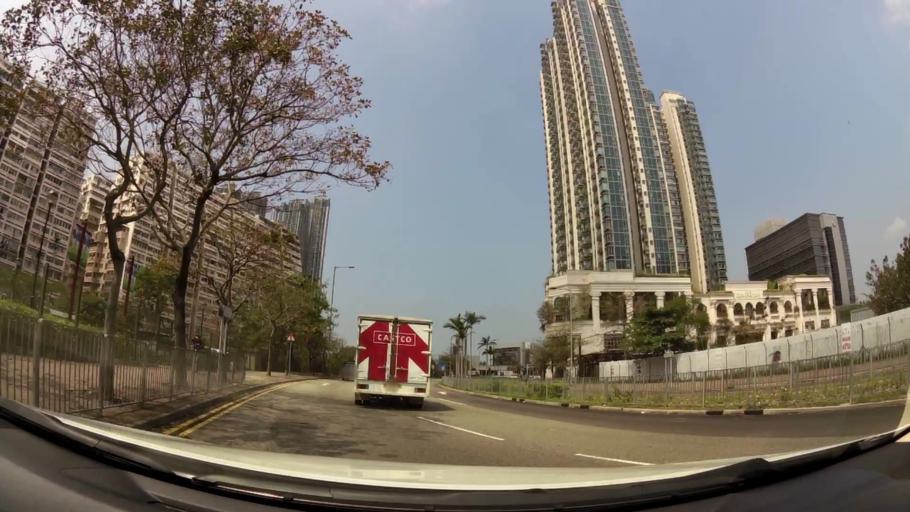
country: HK
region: Kowloon City
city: Kowloon
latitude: 22.3089
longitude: 114.1672
